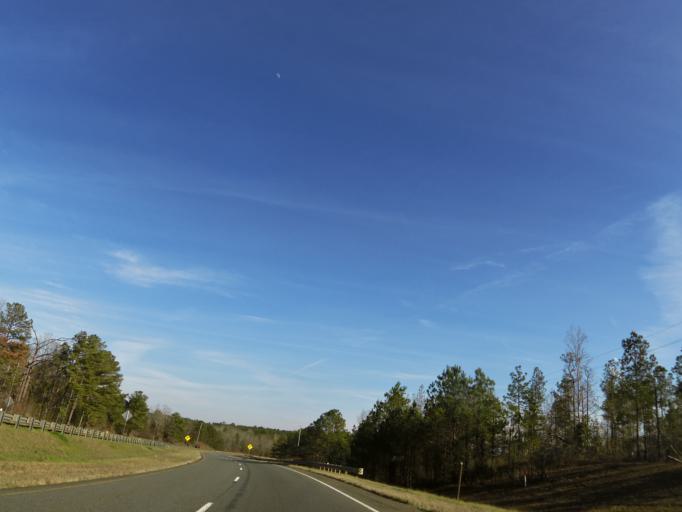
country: US
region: Georgia
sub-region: Stewart County
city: Richland
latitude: 32.1517
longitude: -84.6937
